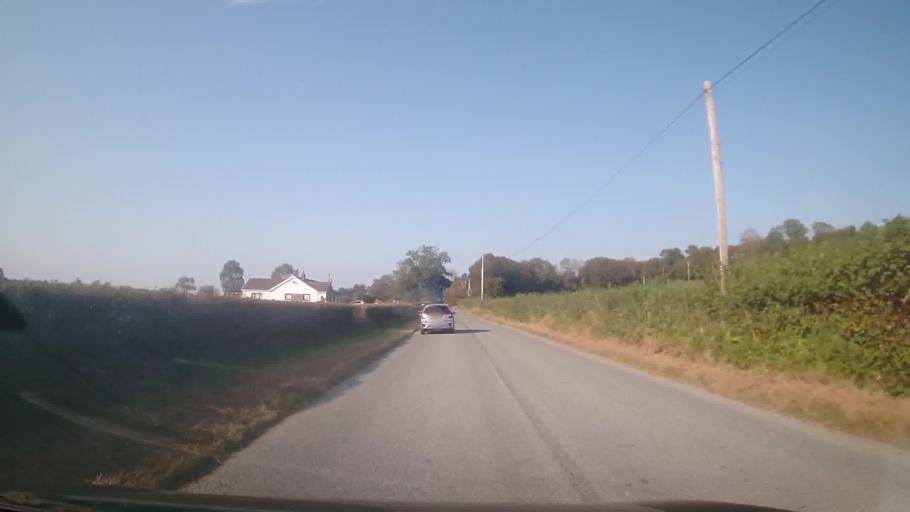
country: GB
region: Wales
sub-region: County of Ceredigion
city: Lledrod
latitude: 52.2266
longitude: -3.9316
